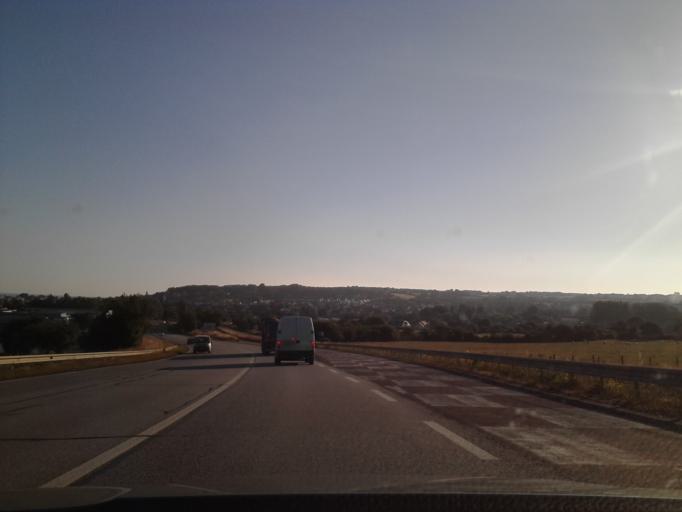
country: FR
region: Lower Normandy
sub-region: Departement de la Manche
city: Tourlaville
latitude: 49.6308
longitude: -1.5792
